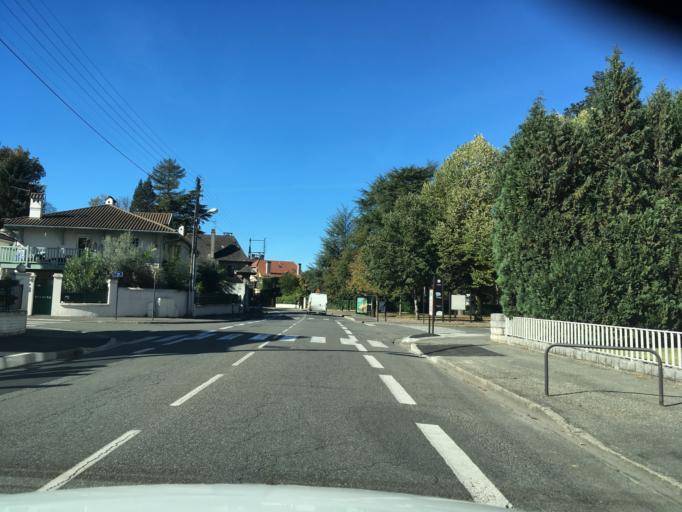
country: FR
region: Aquitaine
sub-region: Departement des Pyrenees-Atlantiques
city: Pau
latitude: 43.2990
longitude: -0.3535
